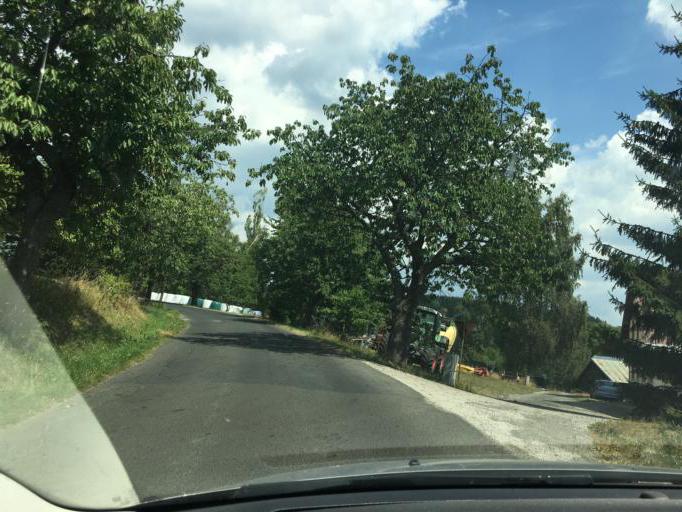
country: CZ
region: Liberecky
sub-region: Okres Semily
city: Ponikla
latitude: 50.6789
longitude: 15.4897
